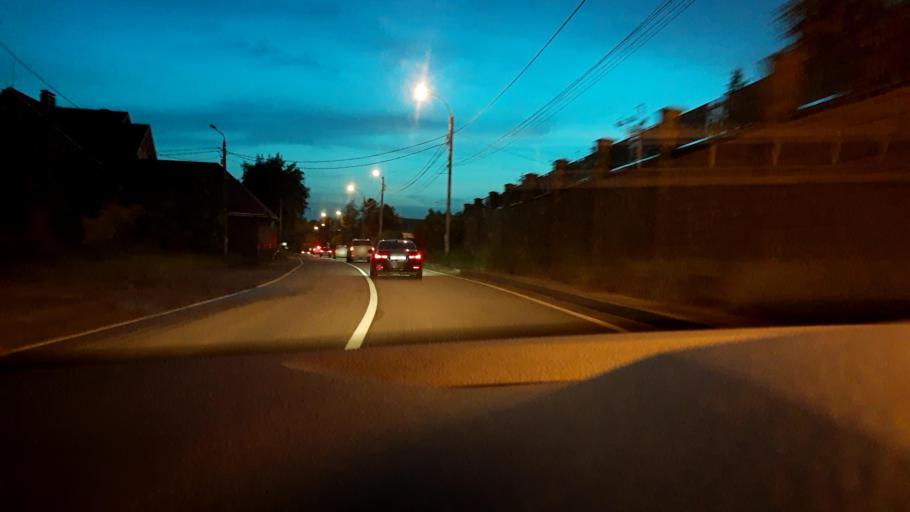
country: RU
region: Moskovskaya
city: Opalikha
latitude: 55.7888
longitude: 37.2234
